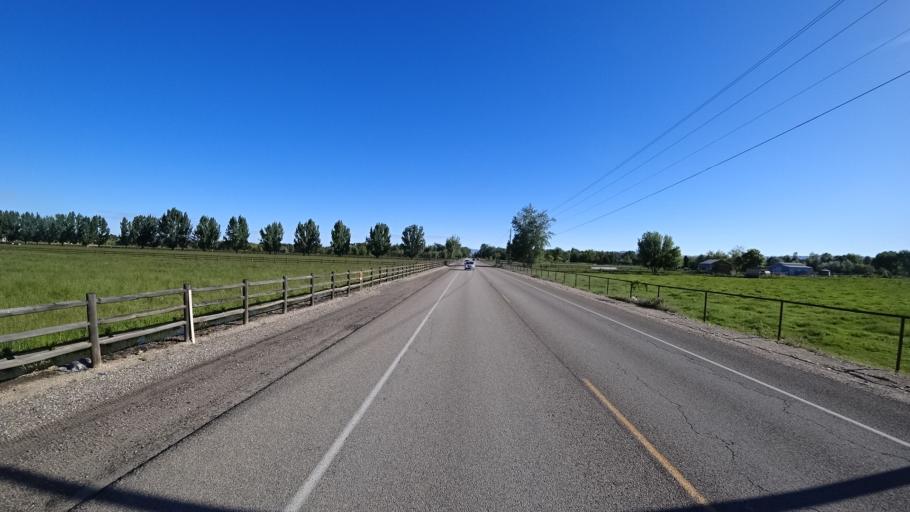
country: US
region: Idaho
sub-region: Ada County
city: Eagle
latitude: 43.6819
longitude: -116.4137
